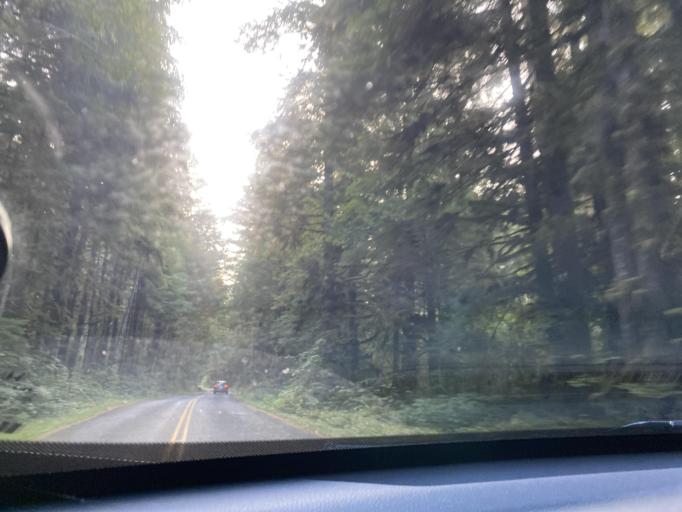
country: US
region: Washington
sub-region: Clallam County
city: Forks
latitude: 47.8164
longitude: -124.0518
